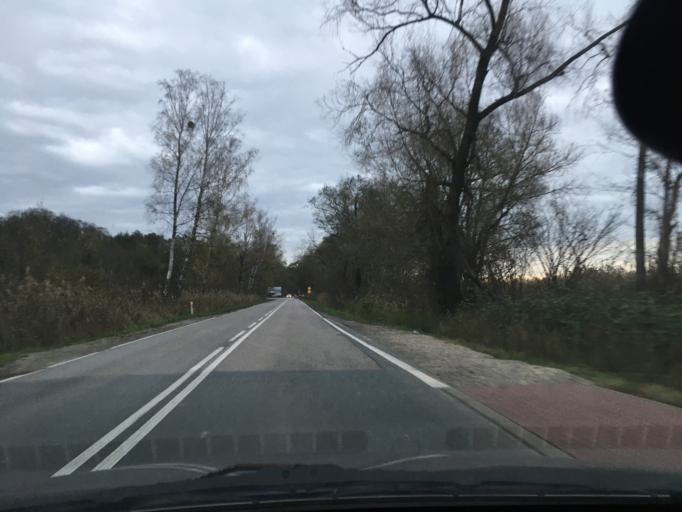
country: PL
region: Masovian Voivodeship
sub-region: Powiat pruszkowski
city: Nadarzyn
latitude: 52.1025
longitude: 20.8405
